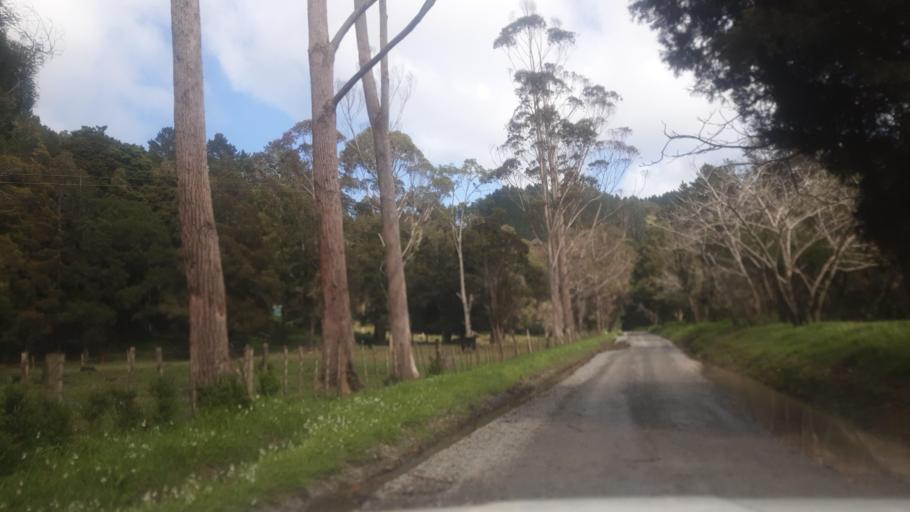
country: NZ
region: Northland
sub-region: Far North District
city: Taipa
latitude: -35.1126
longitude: 173.4297
